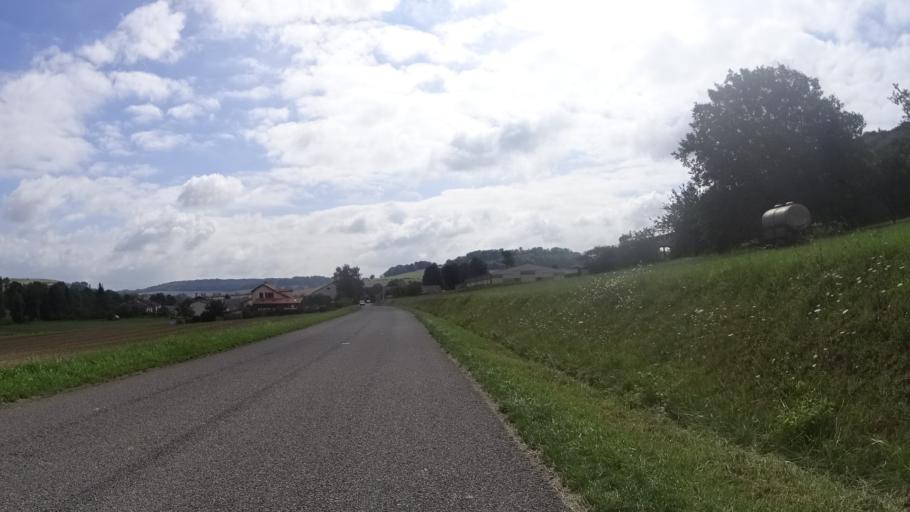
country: FR
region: Lorraine
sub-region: Departement de la Meuse
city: Ligny-en-Barrois
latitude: 48.7162
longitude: 5.3608
